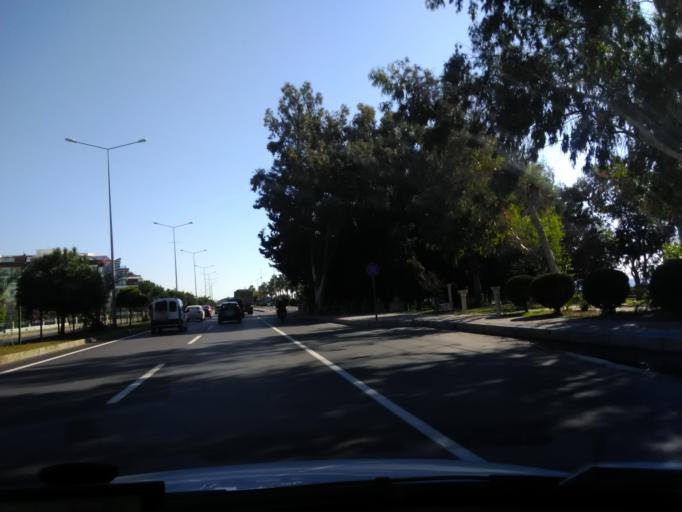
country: TR
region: Antalya
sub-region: Alanya
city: Mahmutlar
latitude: 36.5154
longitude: 32.0630
